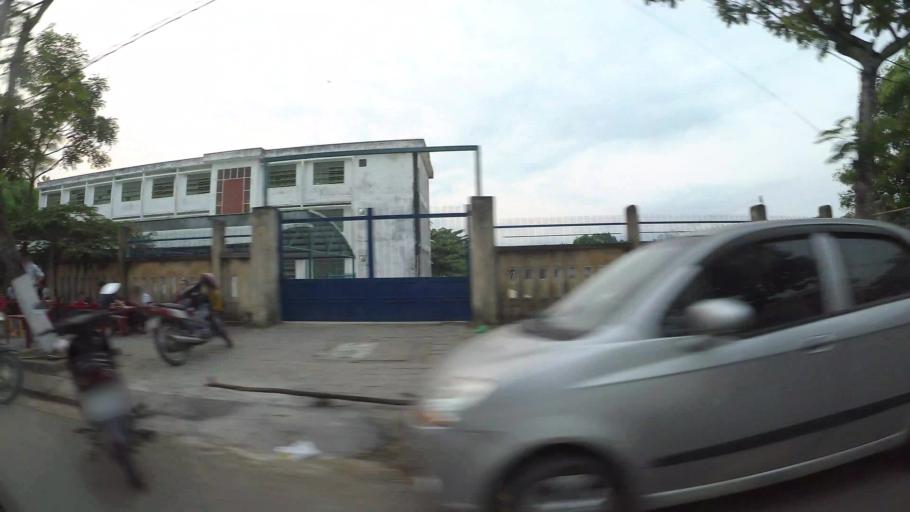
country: VN
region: Da Nang
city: Lien Chieu
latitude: 16.0884
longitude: 108.1458
